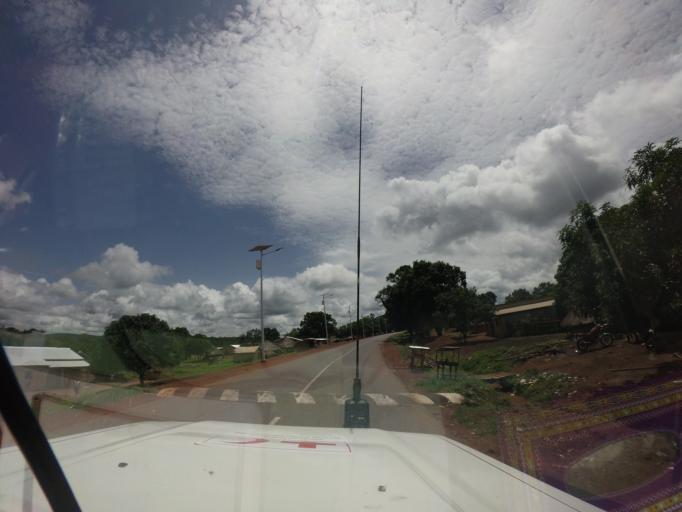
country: SL
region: Northern Province
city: Gberia Fotombu
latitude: 10.0636
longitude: -11.1193
